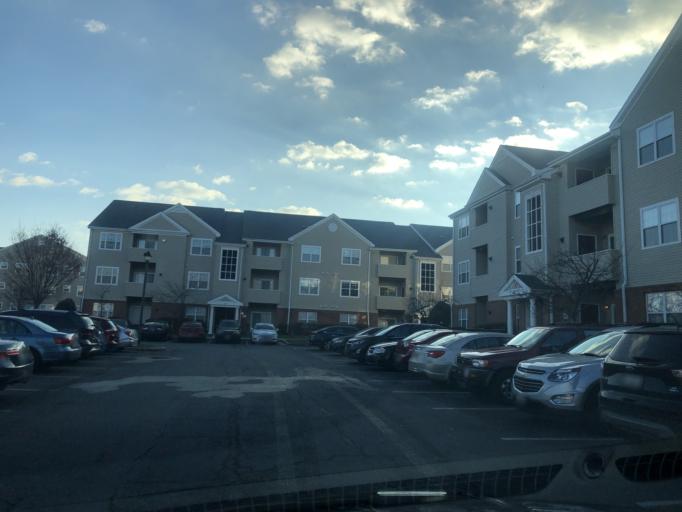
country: US
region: Maryland
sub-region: Anne Arundel County
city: Odenton
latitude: 39.1009
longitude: -76.7154
